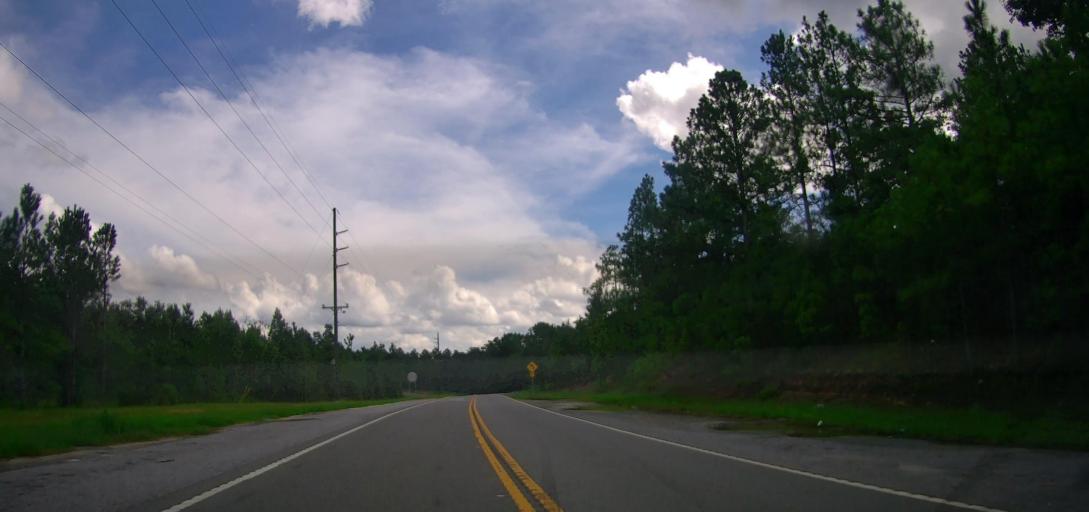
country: US
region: Georgia
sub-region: Talbot County
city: Talbotton
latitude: 32.6142
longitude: -84.4860
